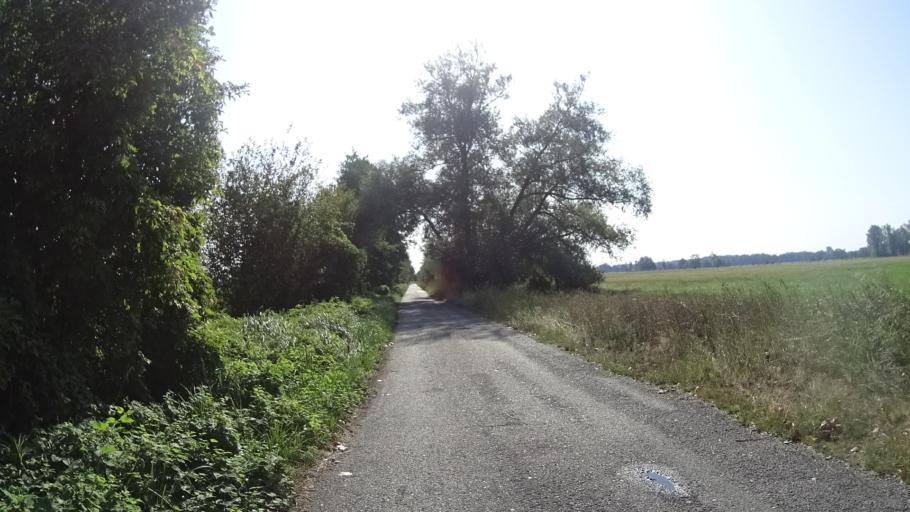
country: DE
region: Brandenburg
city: Neu Zauche
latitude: 51.9026
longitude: 14.0863
